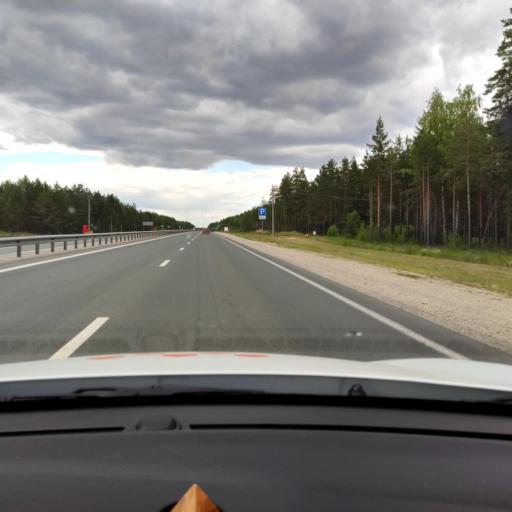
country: RU
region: Mariy-El
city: Surok
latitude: 56.4549
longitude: 48.0962
